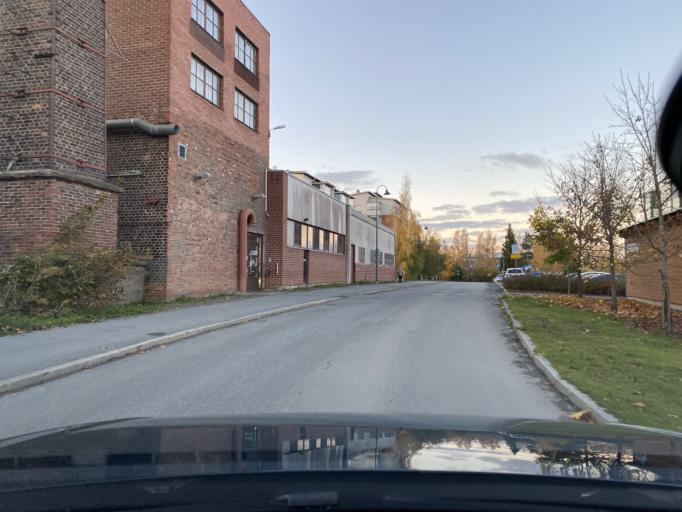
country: FI
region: Pirkanmaa
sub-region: Tampere
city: Lempaeaelae
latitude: 61.3153
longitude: 23.7576
